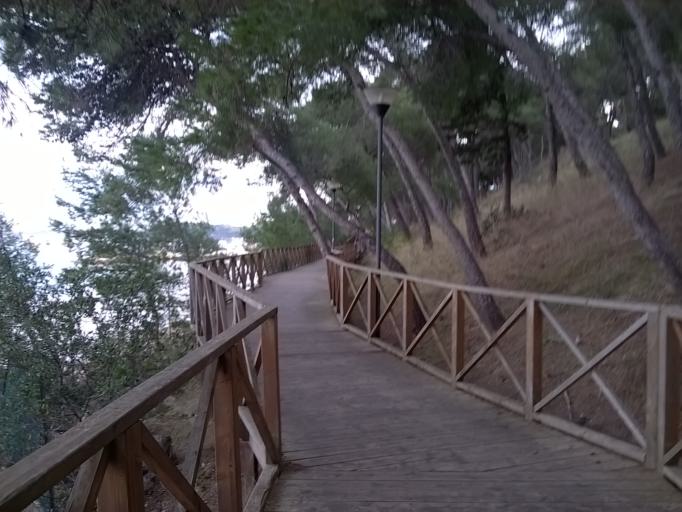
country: IT
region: Apulia
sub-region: Provincia di Taranto
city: Paolo VI
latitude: 40.4688
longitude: 17.2996
